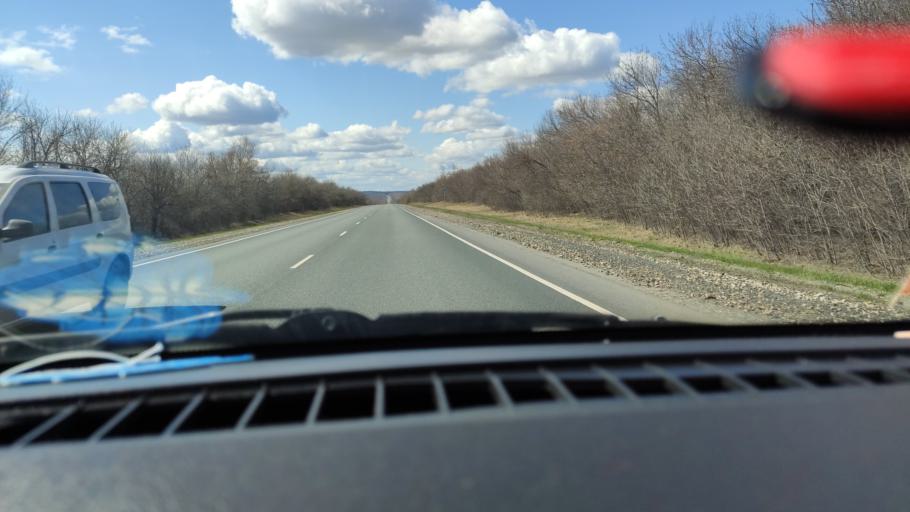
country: RU
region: Saratov
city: Khvalynsk
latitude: 52.5922
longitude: 48.1324
